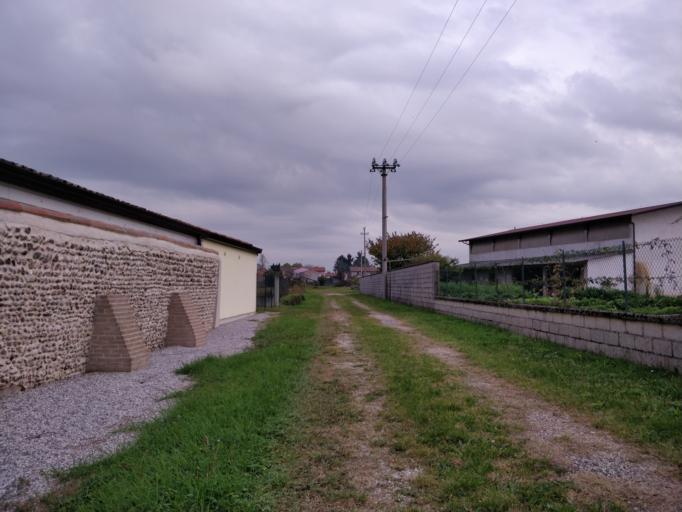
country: IT
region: Friuli Venezia Giulia
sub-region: Provincia di Udine
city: Bertiolo
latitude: 45.9404
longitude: 13.0497
